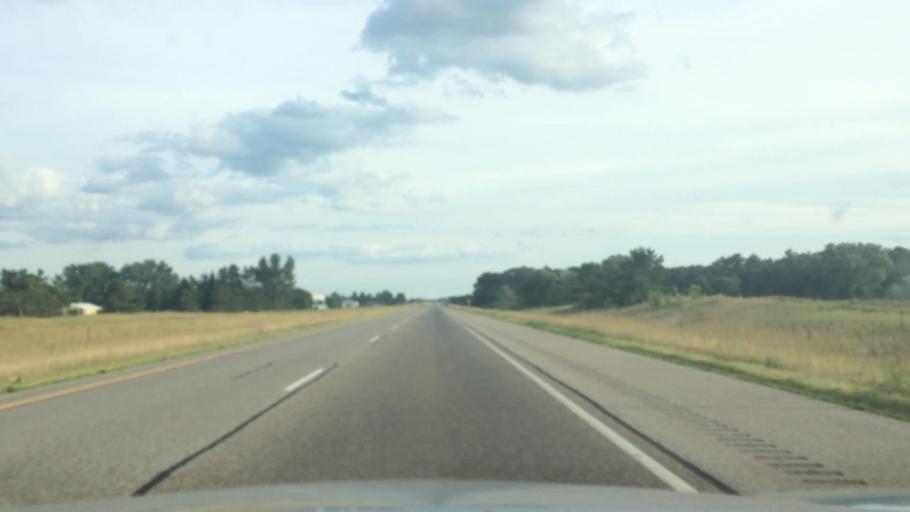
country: US
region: Wisconsin
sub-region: Portage County
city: Plover
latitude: 44.2314
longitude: -89.5246
